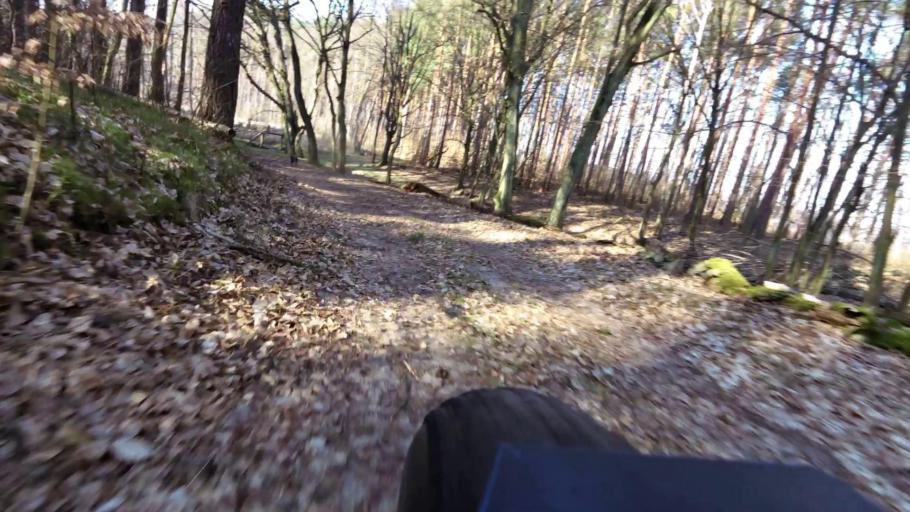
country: PL
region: Lubusz
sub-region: Powiat sulecinski
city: Torzym
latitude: 52.2201
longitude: 14.9687
